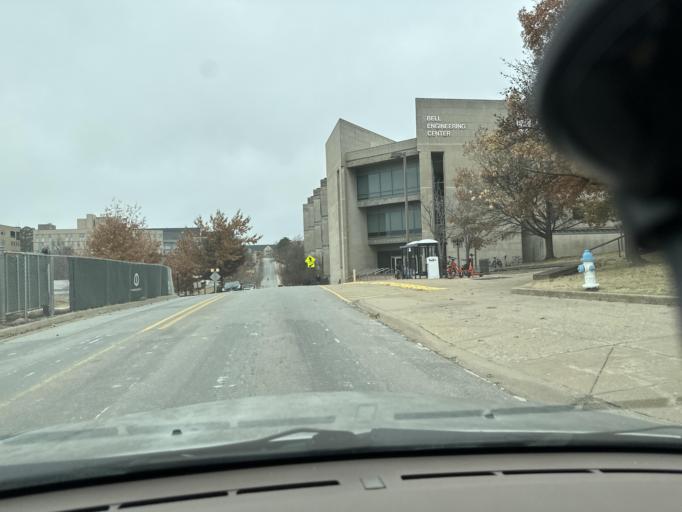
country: US
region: Arkansas
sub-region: Washington County
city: Fayetteville
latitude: 36.0666
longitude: -94.1705
